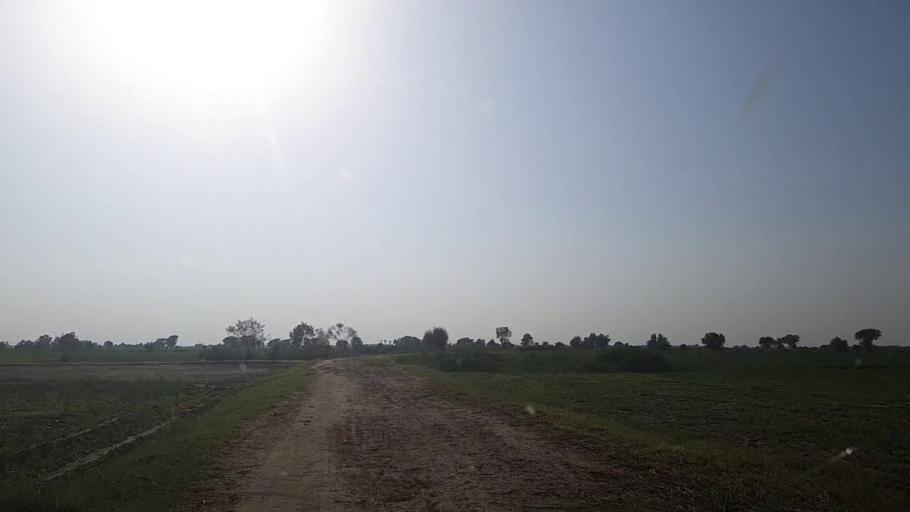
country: PK
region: Sindh
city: Khanpur
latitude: 27.7309
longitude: 69.3271
